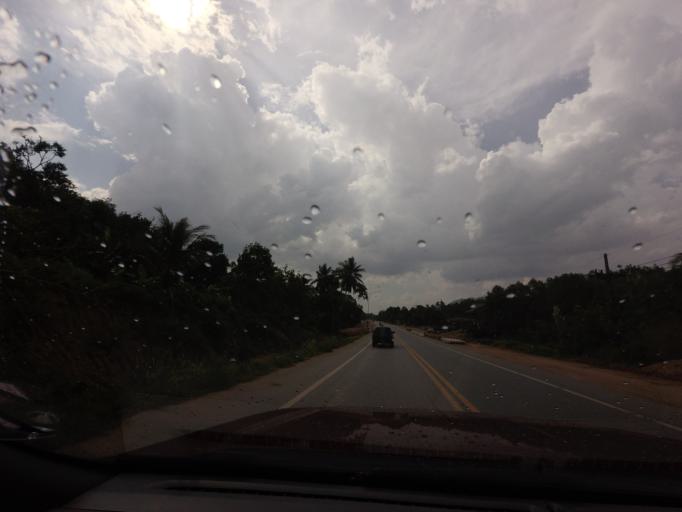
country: TH
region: Yala
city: Krong Pi Nang
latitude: 6.4029
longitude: 101.2818
